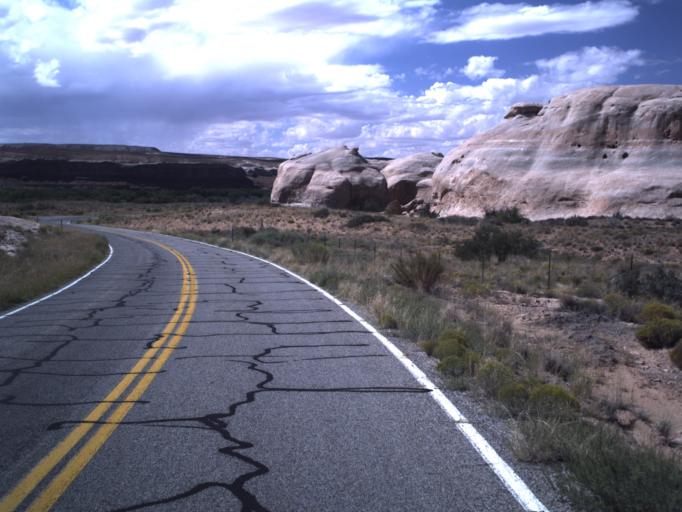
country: US
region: Utah
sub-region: San Juan County
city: Blanding
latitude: 37.2864
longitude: -109.4927
